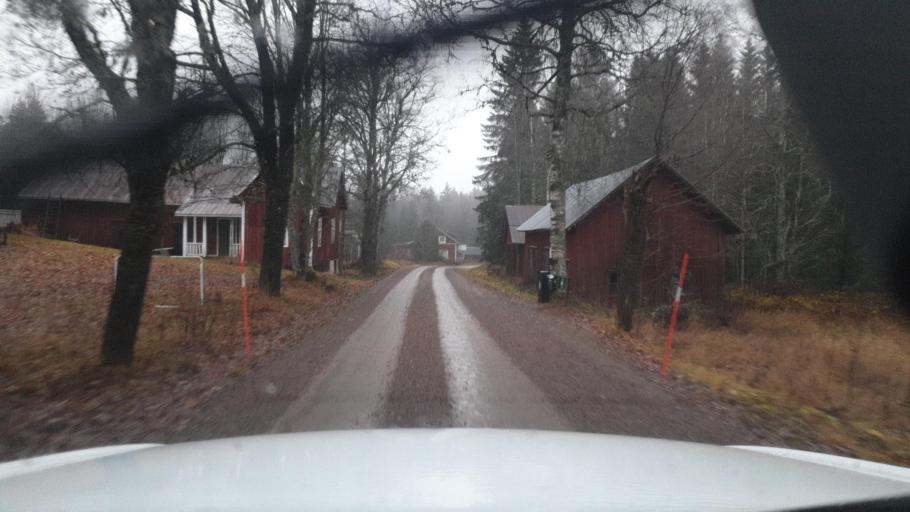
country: SE
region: Vaermland
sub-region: Arvika Kommun
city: Arvika
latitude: 59.9742
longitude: 12.6592
